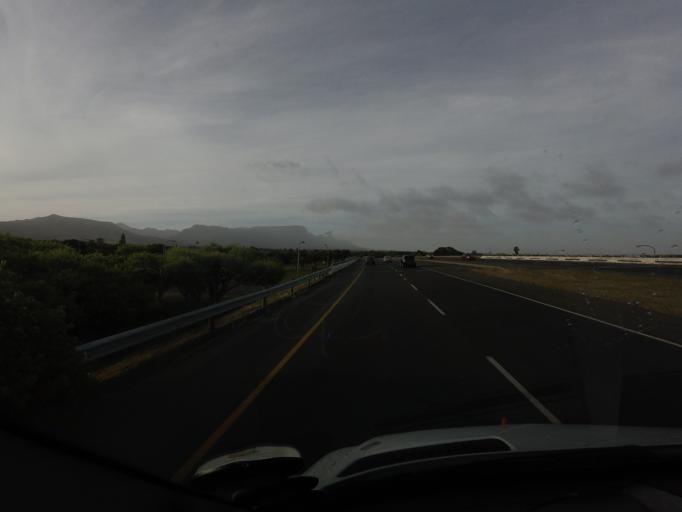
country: ZA
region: Western Cape
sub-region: City of Cape Town
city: Bergvliet
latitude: -34.0652
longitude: 18.4486
